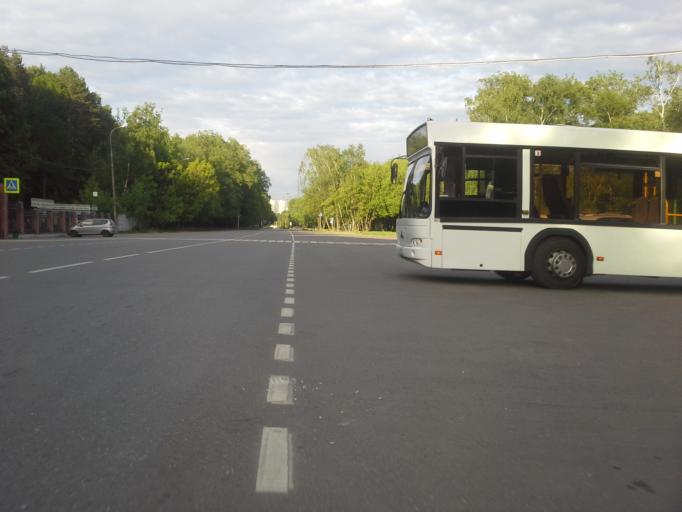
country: RU
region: Moskovskaya
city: Vostryakovo
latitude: 55.6618
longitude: 37.4421
